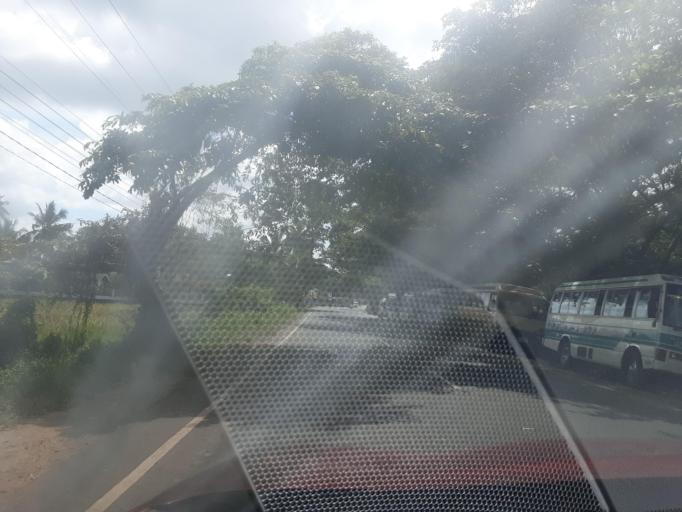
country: LK
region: North Western
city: Kuliyapitiya
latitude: 7.4697
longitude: 80.0497
